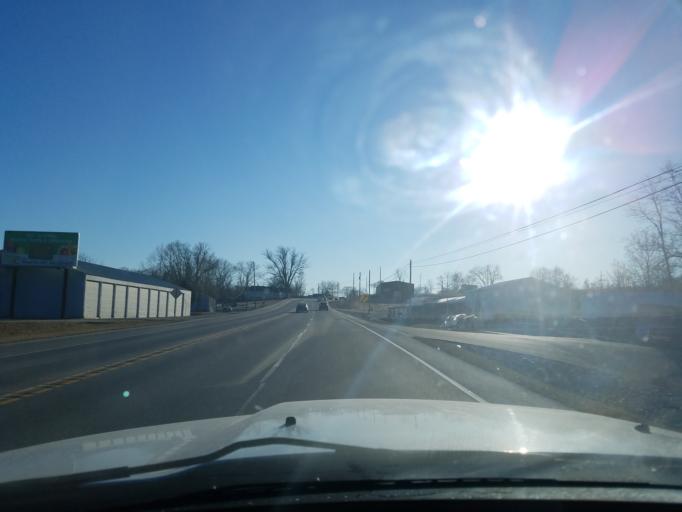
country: US
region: Indiana
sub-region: Orange County
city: Paoli
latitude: 38.5834
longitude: -86.4562
